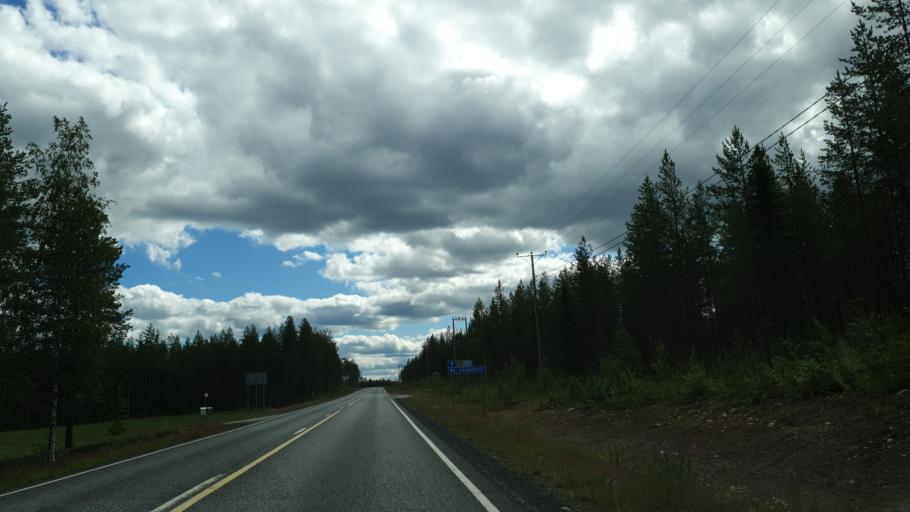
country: FI
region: Kainuu
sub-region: Kehys-Kainuu
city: Kuhmo
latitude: 64.0511
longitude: 29.5527
